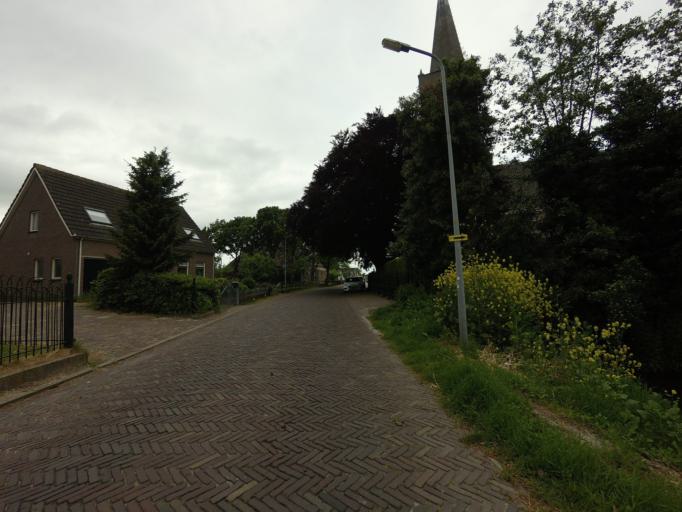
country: NL
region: North Holland
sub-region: Gemeente Hoorn
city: Hoorn
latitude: 52.6796
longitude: 5.0259
